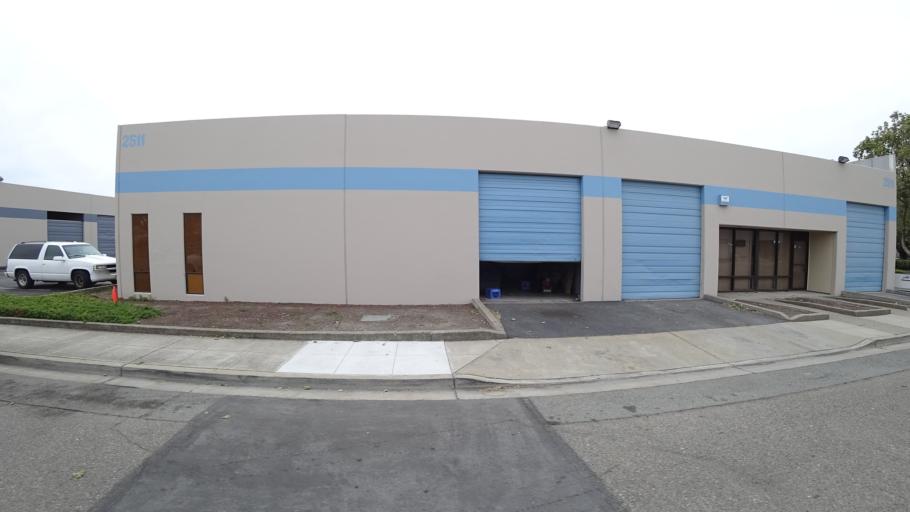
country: US
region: California
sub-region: Alameda County
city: San Lorenzo
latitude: 37.6534
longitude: -122.1388
